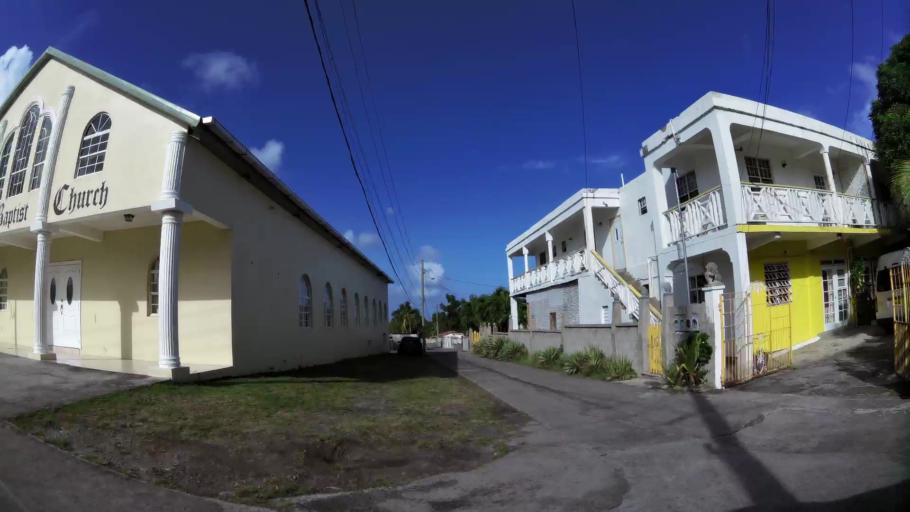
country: KN
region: Saint Paul Charlestown
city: Charlestown
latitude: 17.1412
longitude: -62.6257
